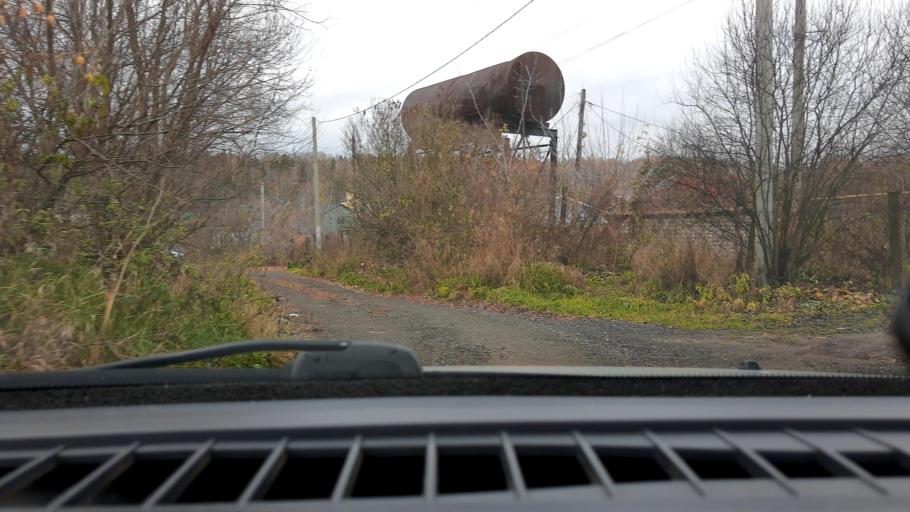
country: RU
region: Nizjnij Novgorod
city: Afonino
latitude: 56.1904
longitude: 44.0812
